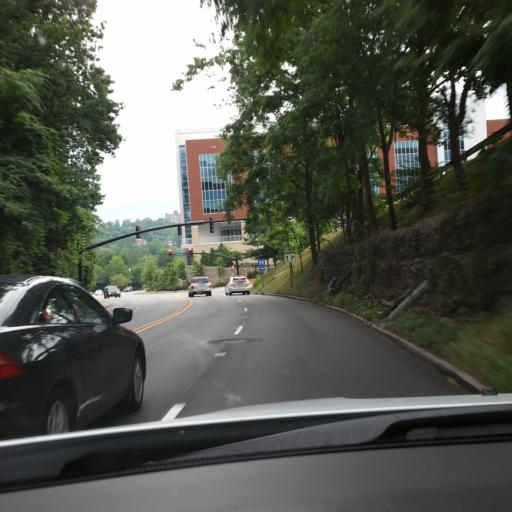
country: US
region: North Carolina
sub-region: Buncombe County
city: Asheville
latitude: 35.5779
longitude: -82.5516
